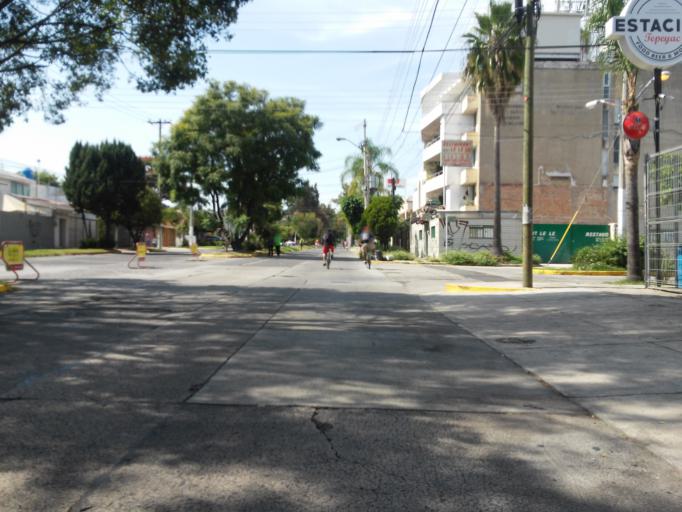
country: MX
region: Jalisco
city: Guadalajara
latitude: 20.6584
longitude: -103.4157
